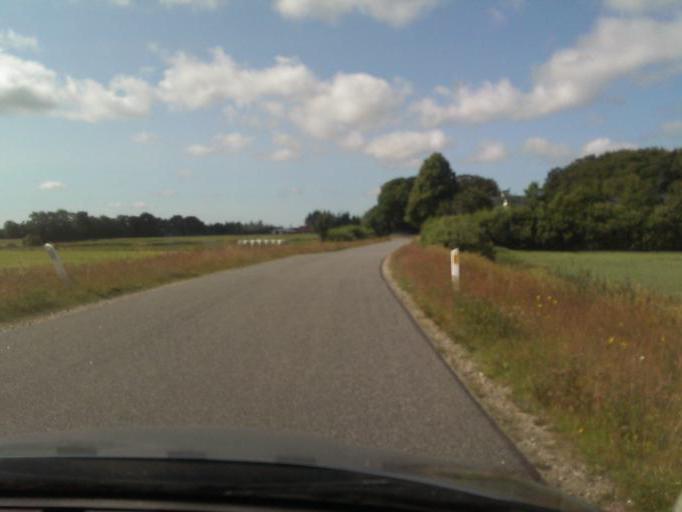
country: DK
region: North Denmark
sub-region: Alborg Kommune
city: Vestbjerg
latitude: 57.1959
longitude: 9.9292
